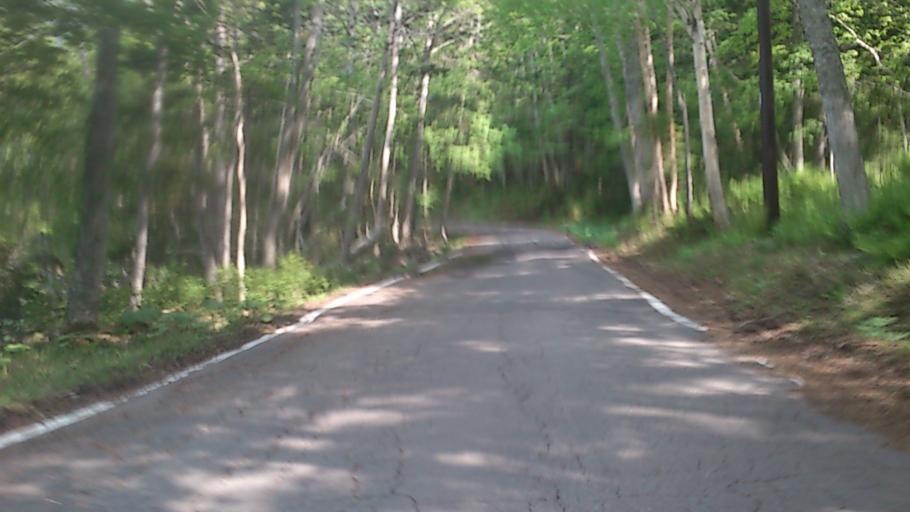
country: JP
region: Hokkaido
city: Kitami
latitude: 43.3819
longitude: 143.9668
